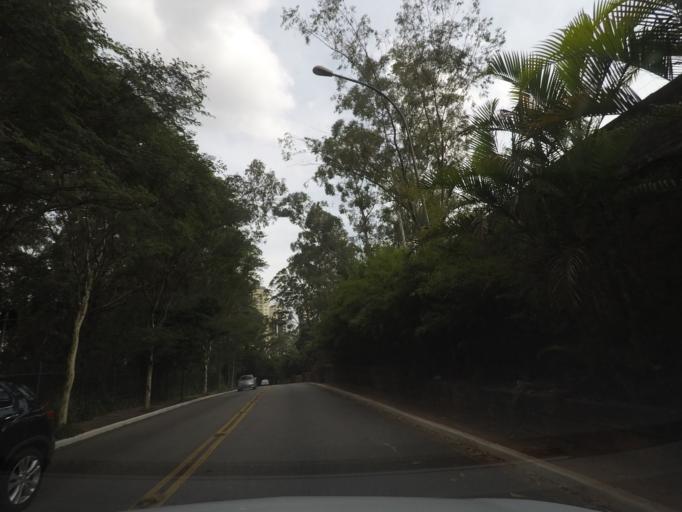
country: BR
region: Sao Paulo
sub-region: Taboao Da Serra
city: Taboao da Serra
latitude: -23.6300
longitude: -46.7235
